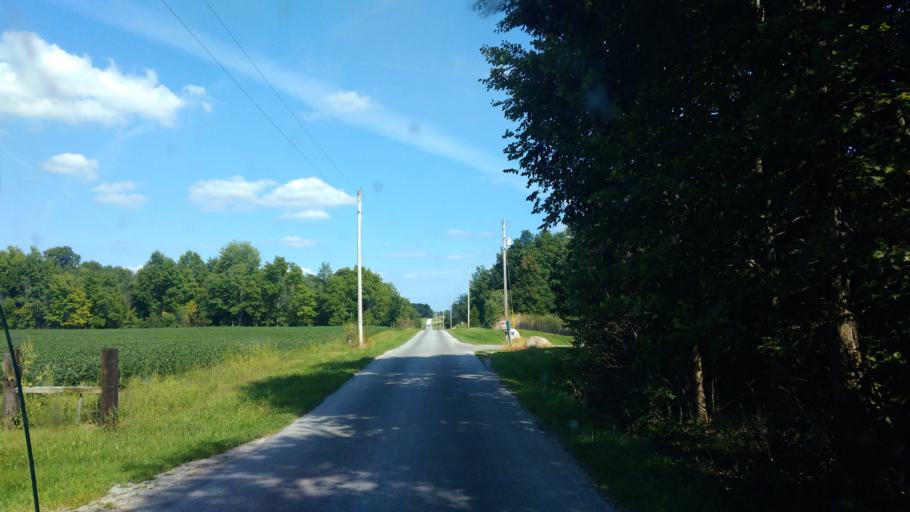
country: US
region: Ohio
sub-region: Hardin County
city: Kenton
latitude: 40.6288
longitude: -83.4640
